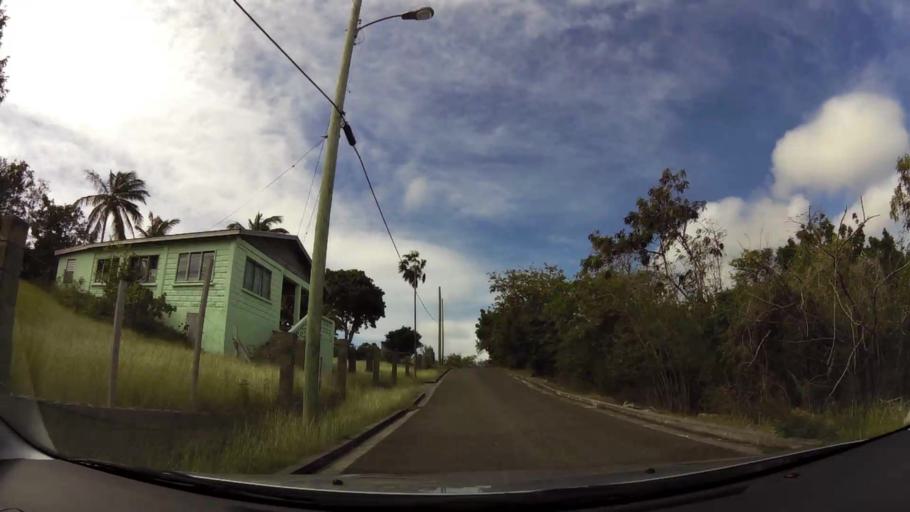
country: AG
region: Saint Paul
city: Falmouth
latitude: 17.0465
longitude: -61.7256
